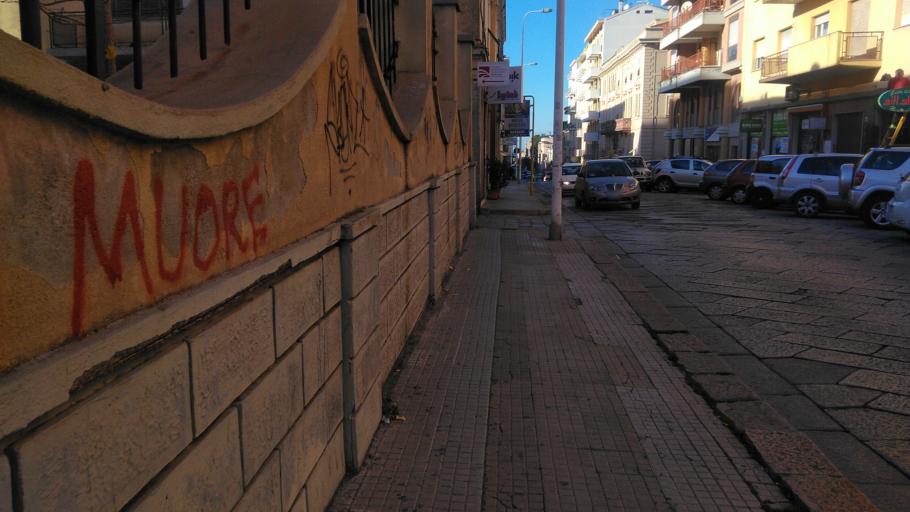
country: IT
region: Sardinia
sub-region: Provincia di Sassari
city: Sassari
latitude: 40.7192
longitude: 8.5703
